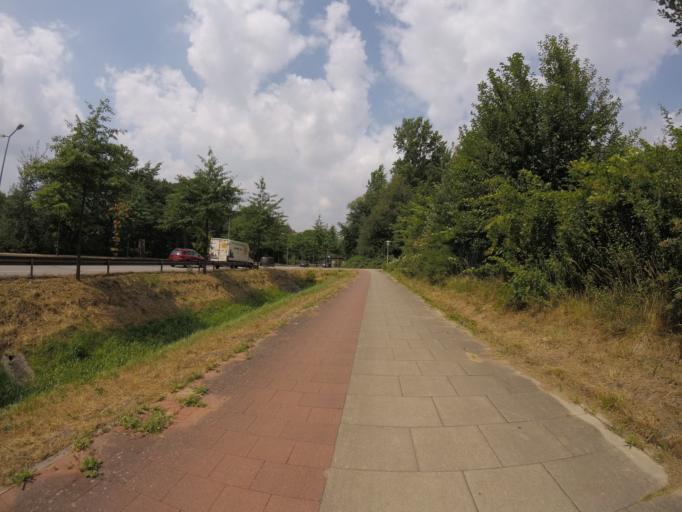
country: DE
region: Hamburg
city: Alsterdorf
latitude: 53.6085
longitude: 10.0259
